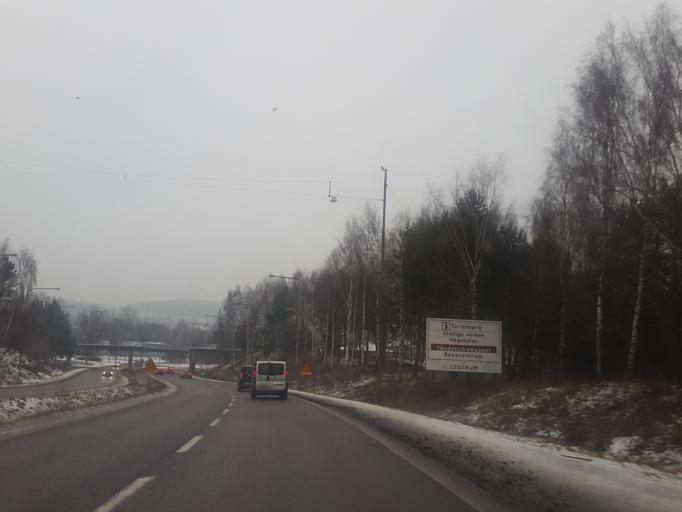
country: SE
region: Joenkoeping
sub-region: Jonkopings Kommun
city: Jonkoping
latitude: 57.7611
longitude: 14.1558
